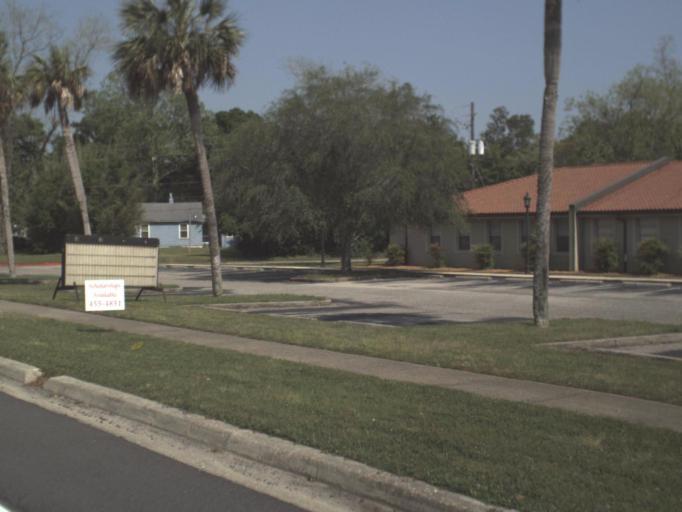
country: US
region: Florida
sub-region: Escambia County
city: Myrtle Grove
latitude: 30.4229
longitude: -87.2996
